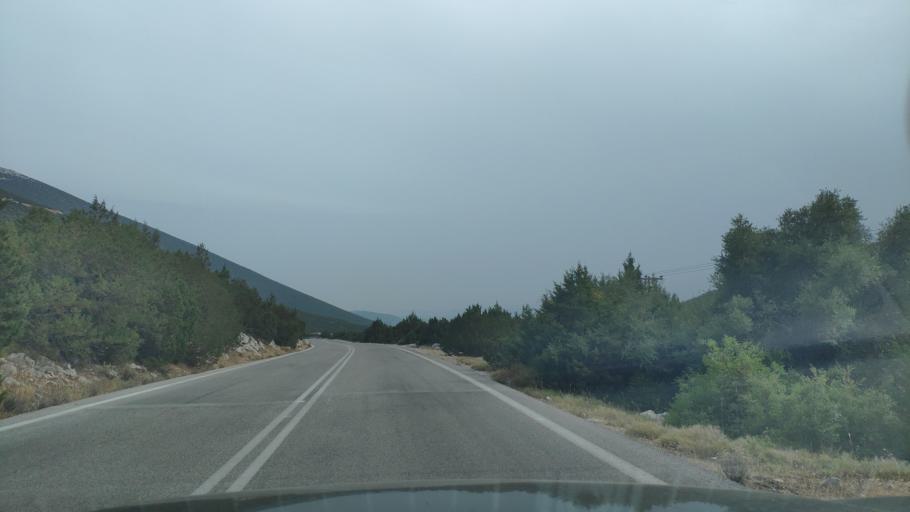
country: GR
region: Peloponnese
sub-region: Nomos Argolidos
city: Didyma
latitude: 37.5007
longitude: 23.1907
